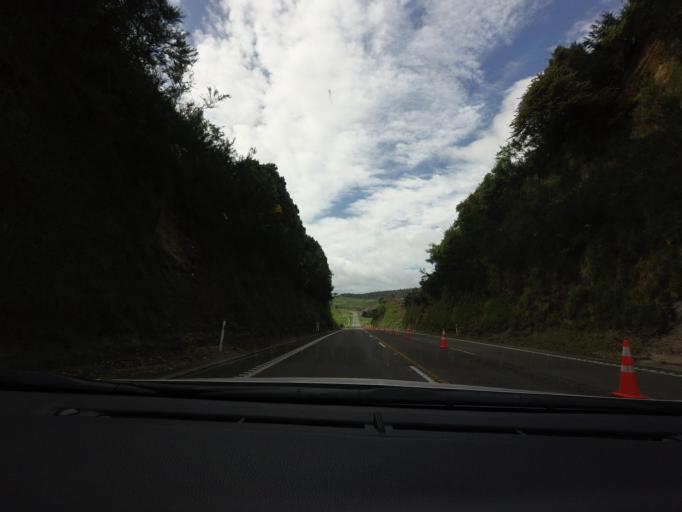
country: NZ
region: Bay of Plenty
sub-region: Rotorua District
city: Rotorua
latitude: -38.2513
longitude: 176.3181
